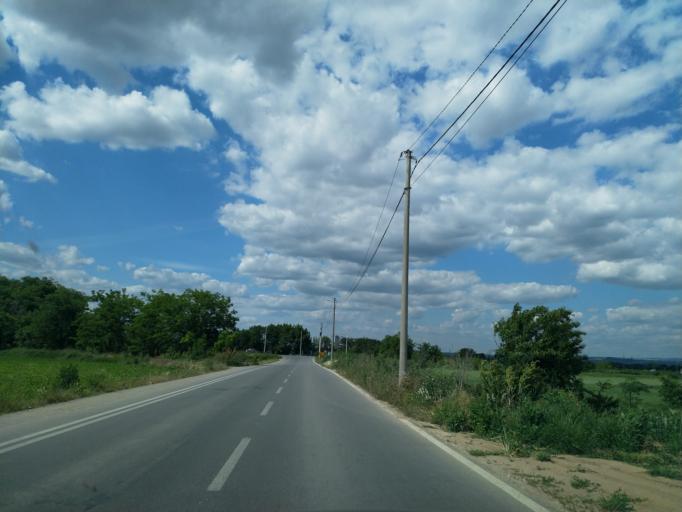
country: RS
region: Central Serbia
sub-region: Pomoravski Okrug
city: Jagodina
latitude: 43.9561
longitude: 21.2910
